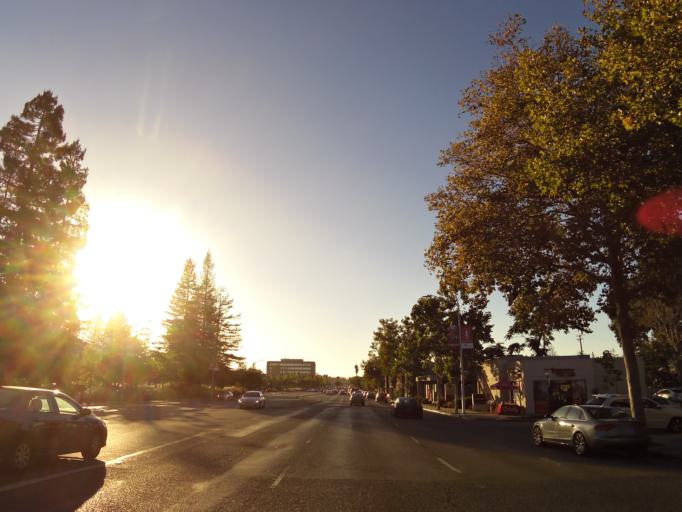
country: US
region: California
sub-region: Santa Clara County
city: Palo Alto
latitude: 37.4220
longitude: -122.1399
